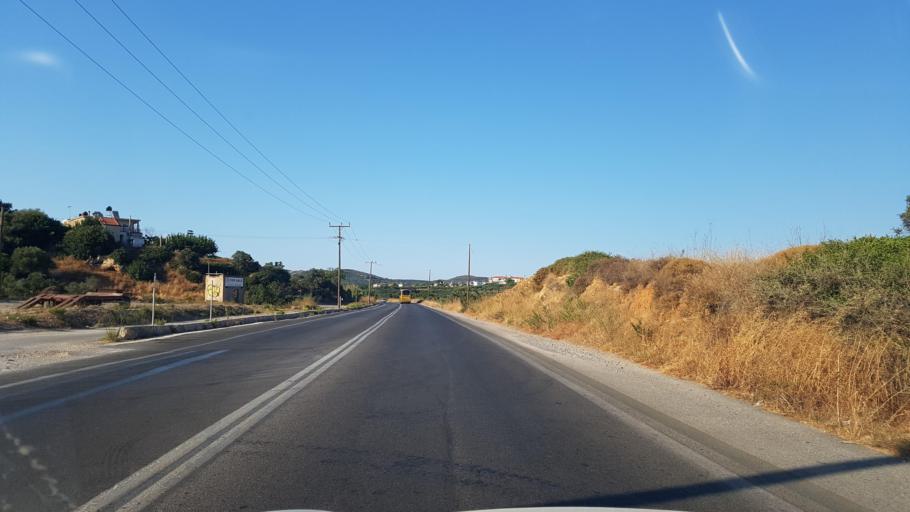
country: GR
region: Crete
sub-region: Nomos Chanias
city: Kolympari
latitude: 35.5203
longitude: 23.7453
